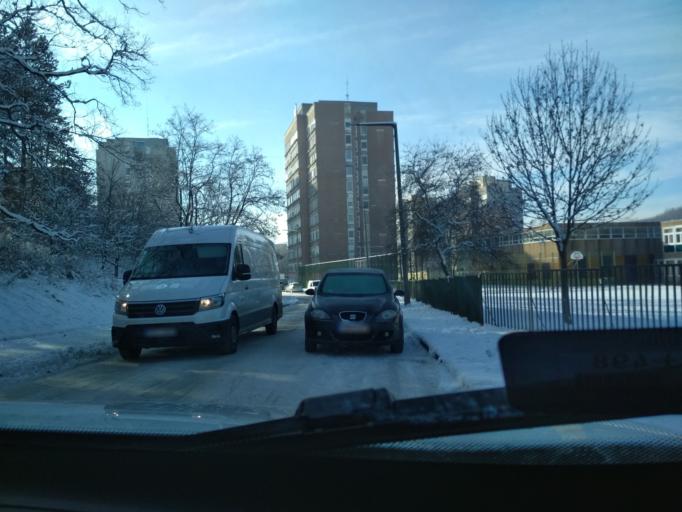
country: HU
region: Nograd
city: Salgotarjan
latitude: 48.1294
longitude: 19.8151
